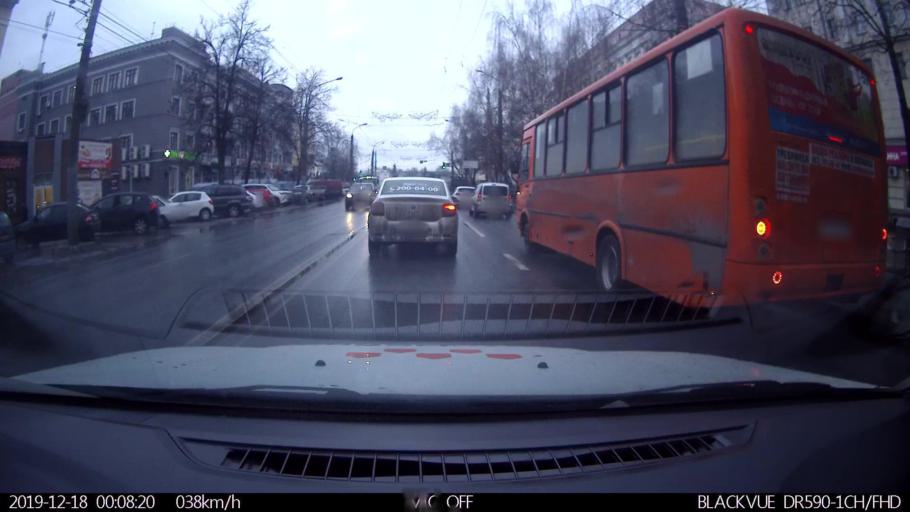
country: RU
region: Nizjnij Novgorod
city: Neklyudovo
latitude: 56.3509
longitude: 43.8677
